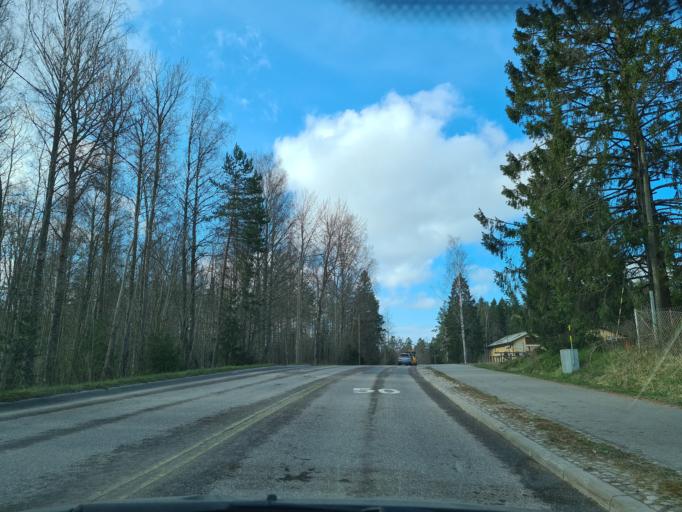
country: FI
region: Uusimaa
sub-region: Helsinki
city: Kirkkonummi
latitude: 60.0859
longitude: 24.4076
